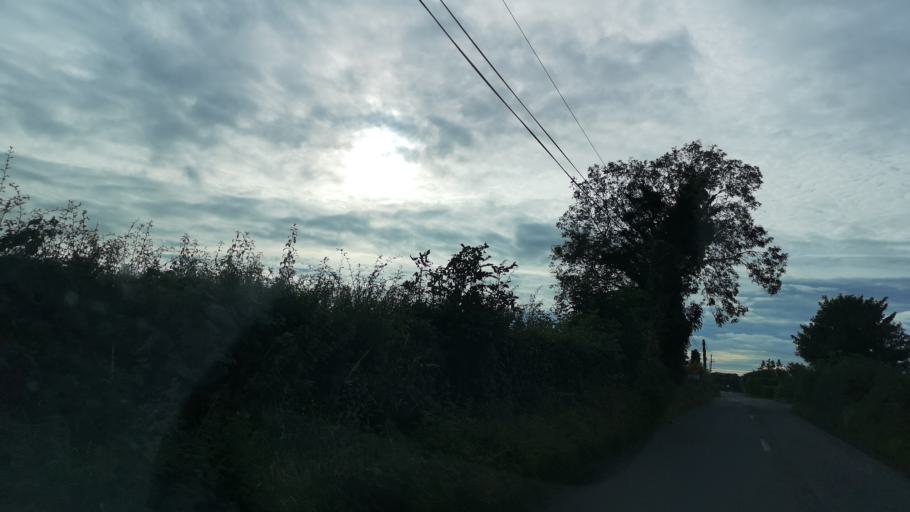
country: IE
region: Connaught
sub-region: County Galway
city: Ballinasloe
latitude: 53.3584
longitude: -8.2099
